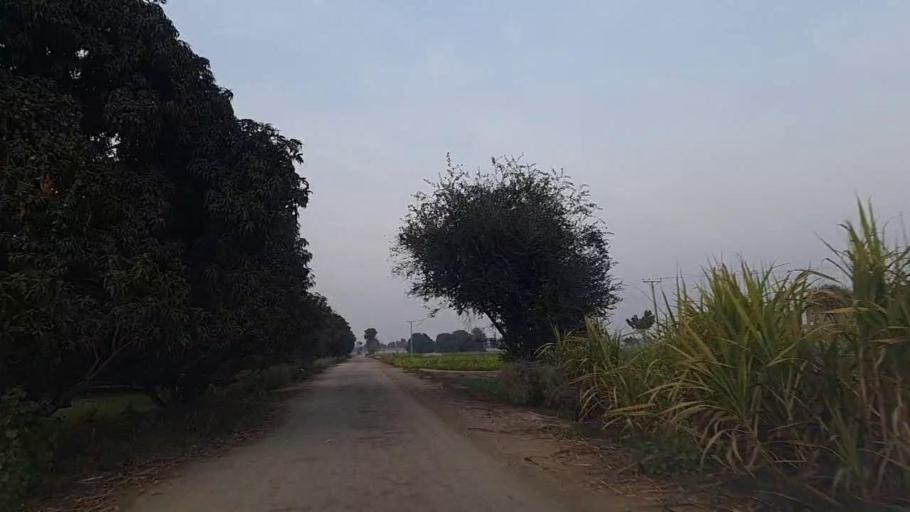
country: PK
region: Sindh
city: Jam Sahib
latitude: 26.4661
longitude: 68.5480
